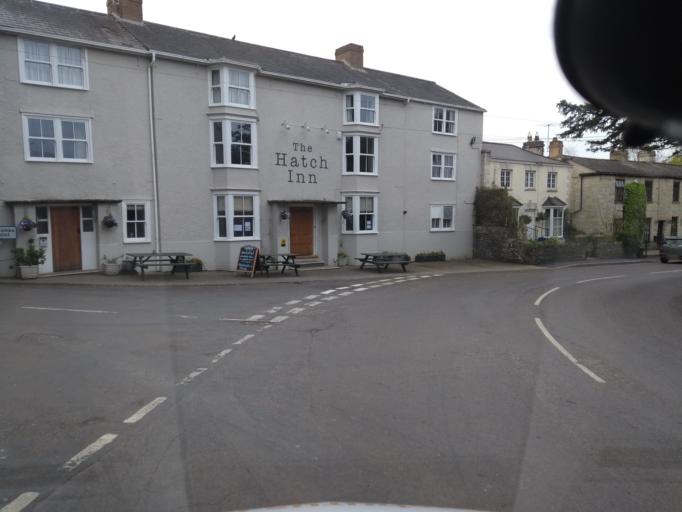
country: GB
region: England
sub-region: Somerset
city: Creech Saint Michael
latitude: 50.9804
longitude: -2.9952
